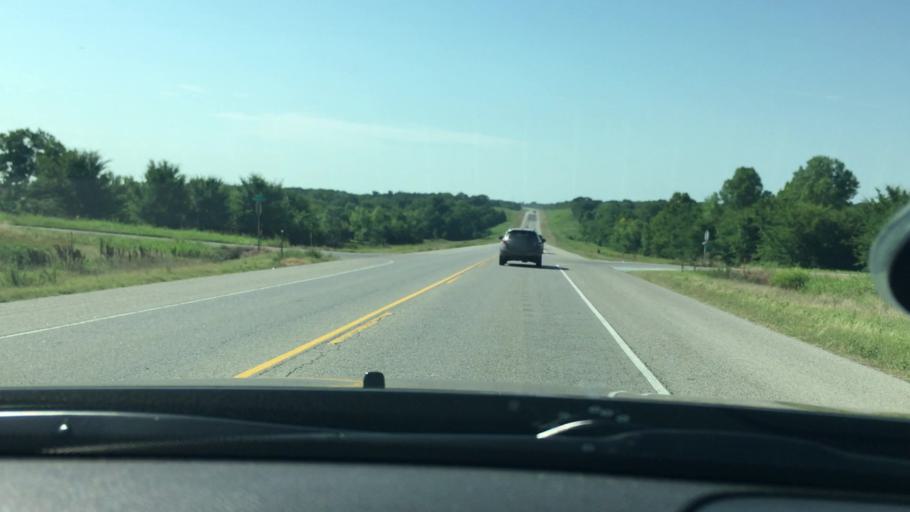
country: US
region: Oklahoma
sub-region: Pontotoc County
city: Ada
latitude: 34.6661
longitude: -96.5657
